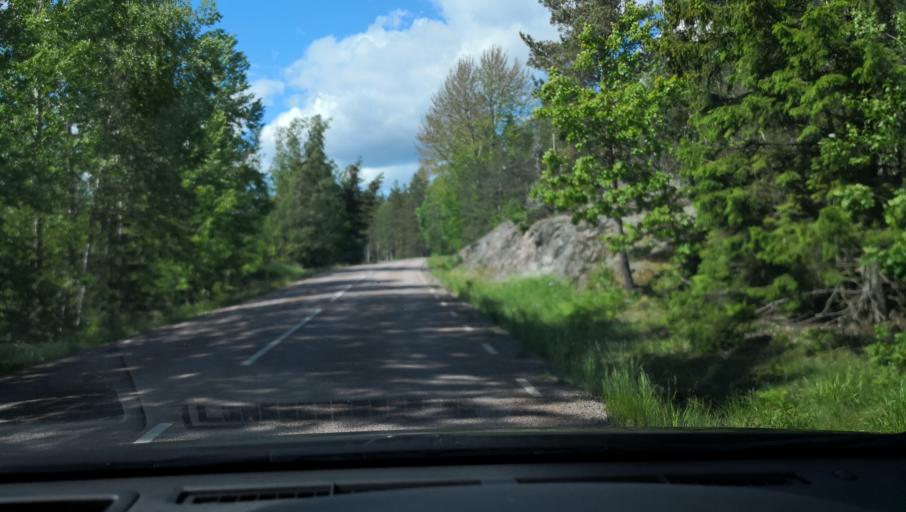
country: SE
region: Vaestmanland
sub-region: Arboga Kommun
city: Tyringe
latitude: 59.3029
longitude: 16.0164
